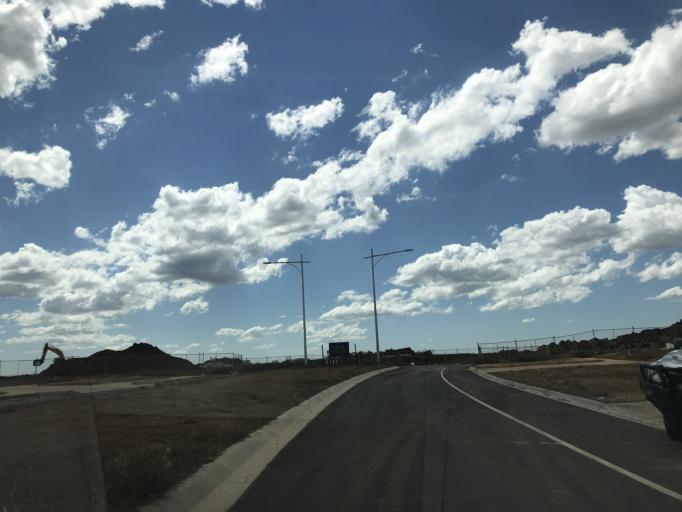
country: AU
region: Victoria
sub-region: Wyndham
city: Truganina
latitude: -37.8159
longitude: 144.7118
